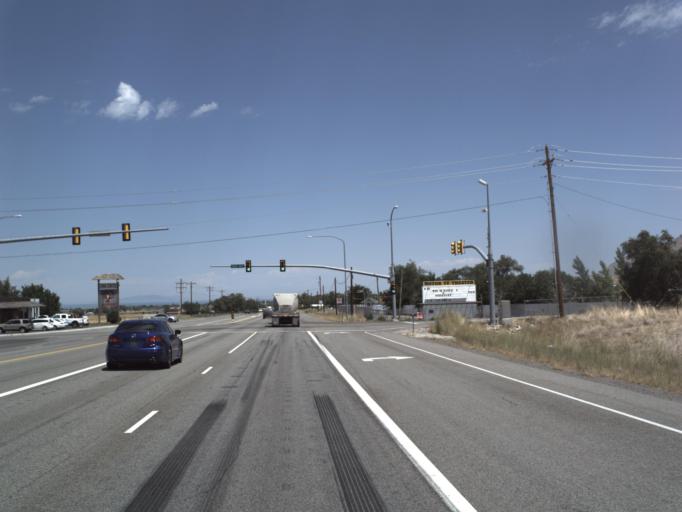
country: US
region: Utah
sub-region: Tooele County
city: Erda
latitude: 40.5981
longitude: -112.2941
